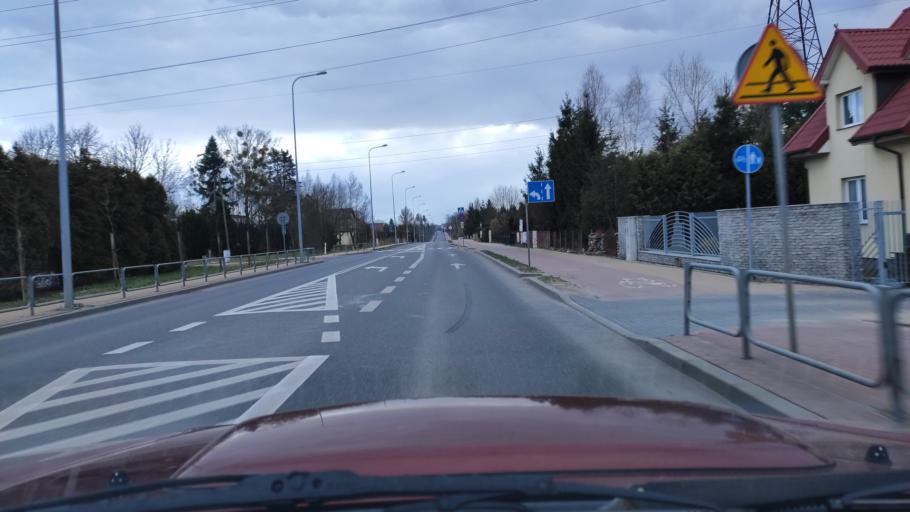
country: PL
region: Masovian Voivodeship
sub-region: Powiat zwolenski
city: Zwolen
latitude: 51.3692
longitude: 21.5859
